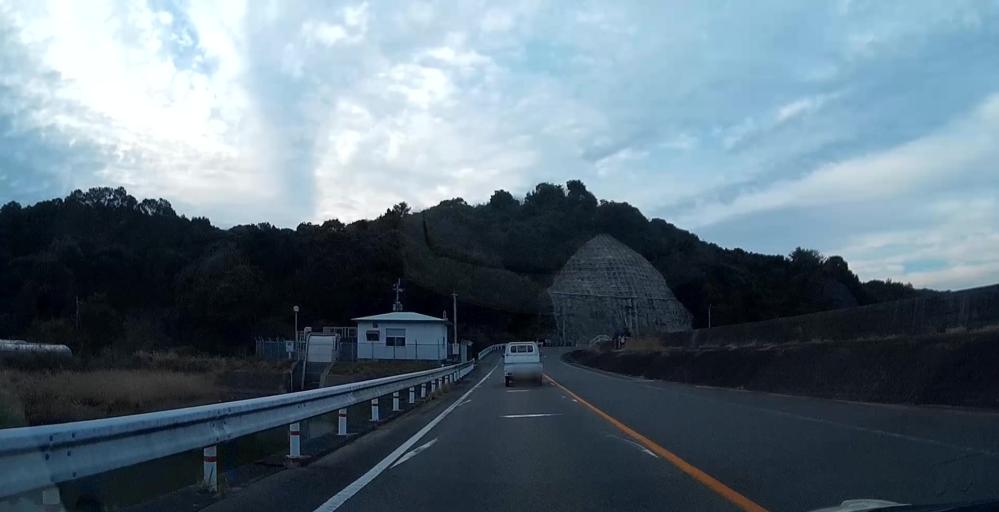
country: JP
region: Kumamoto
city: Hondo
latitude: 32.5005
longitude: 130.3920
